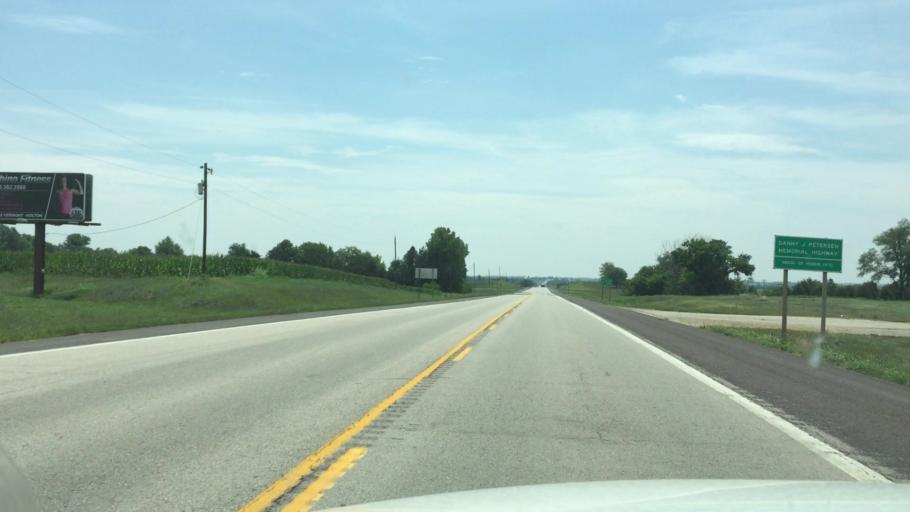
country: US
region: Kansas
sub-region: Jackson County
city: Holton
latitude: 39.6126
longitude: -95.7313
